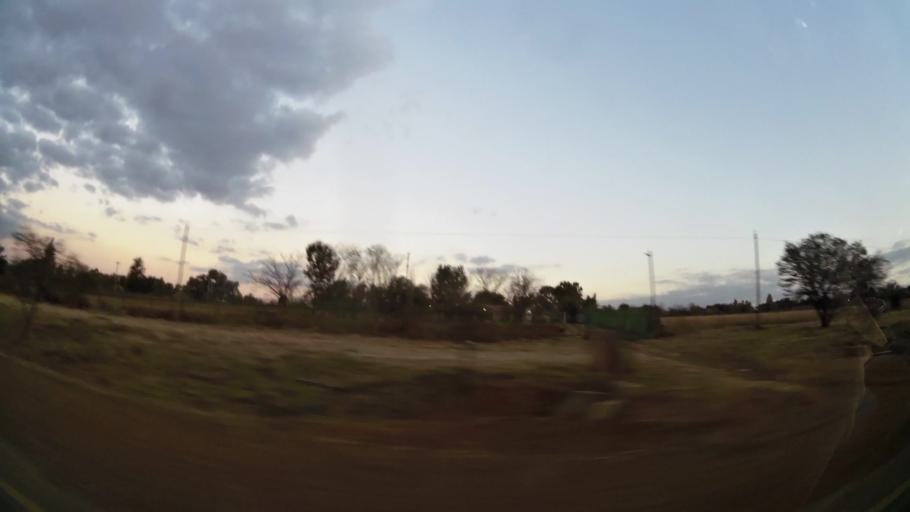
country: ZA
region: Gauteng
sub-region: West Rand District Municipality
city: Krugersdorp
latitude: -26.0683
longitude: 27.6871
